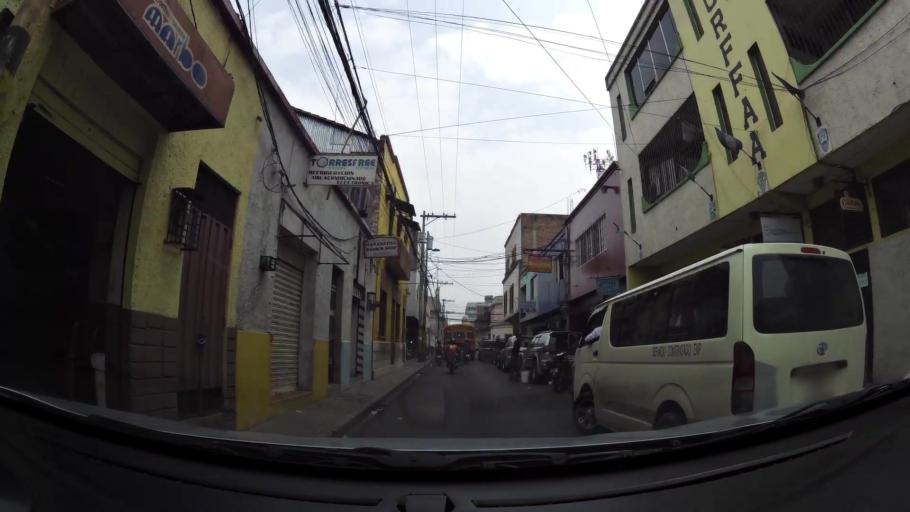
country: HN
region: Francisco Morazan
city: Tegucigalpa
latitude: 14.1000
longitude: -87.2073
